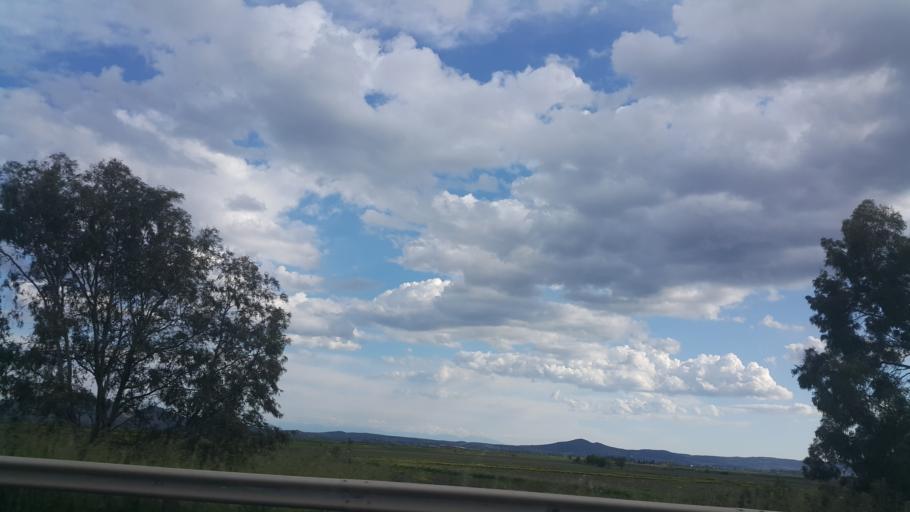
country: TR
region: Adana
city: Ceyhan
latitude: 36.9828
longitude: 35.8411
